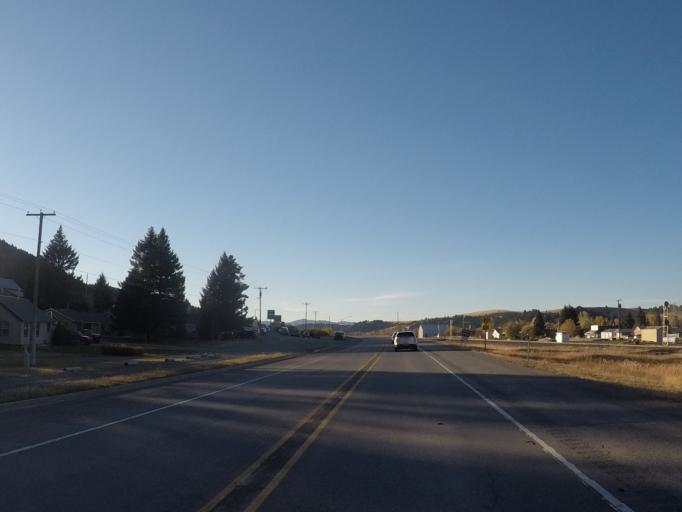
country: US
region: Montana
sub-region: Lewis and Clark County
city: Helena West Side
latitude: 46.5602
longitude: -112.4276
